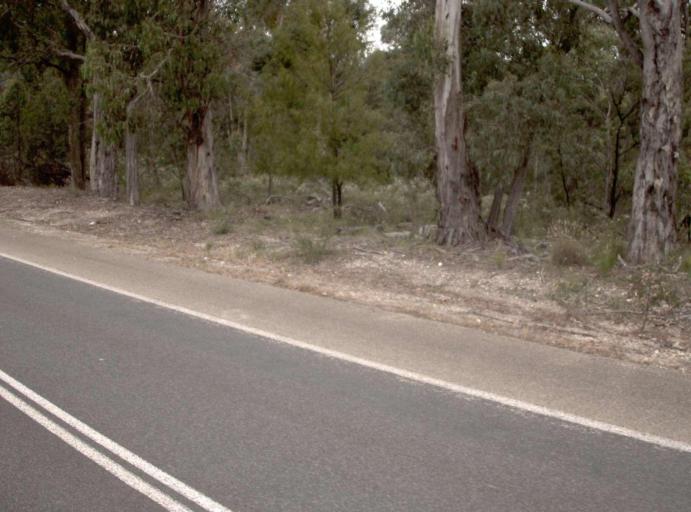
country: AU
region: Victoria
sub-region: East Gippsland
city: Lakes Entrance
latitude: -37.7219
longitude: 147.8737
